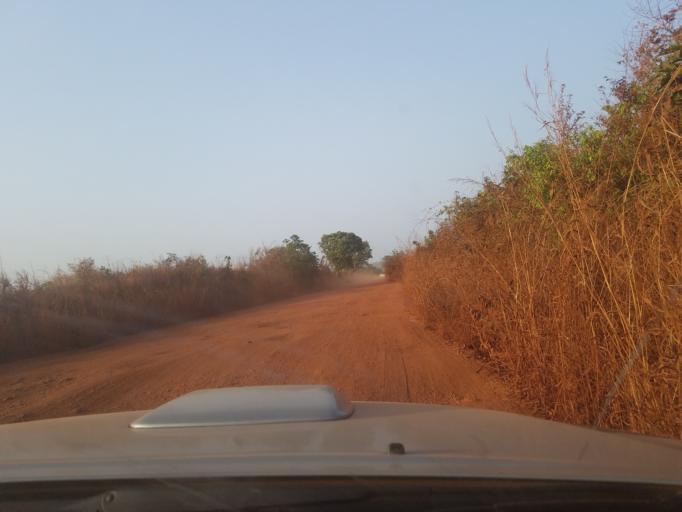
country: GN
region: Boke
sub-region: Gaoual Prefecture
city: Gaoual
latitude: 11.5048
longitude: -13.8599
